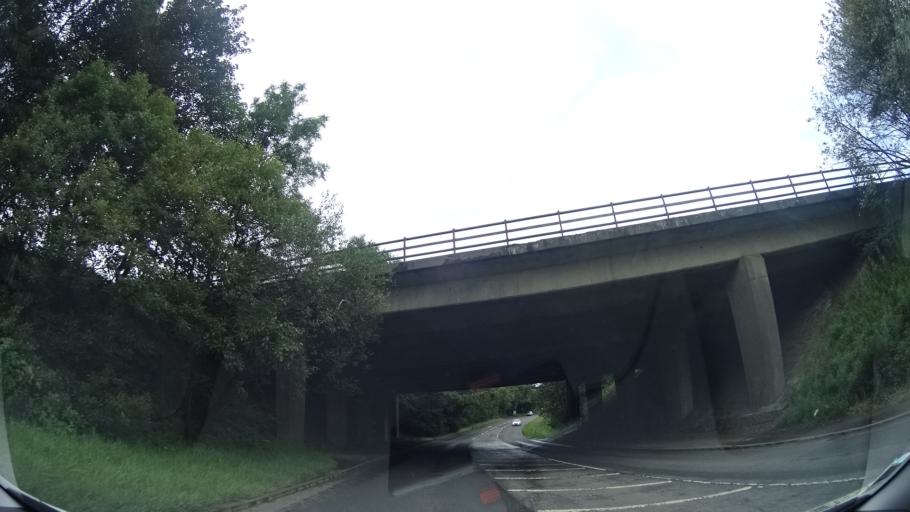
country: GB
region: Scotland
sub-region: Falkirk
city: Bonnybridge
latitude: 56.0133
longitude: -3.8757
